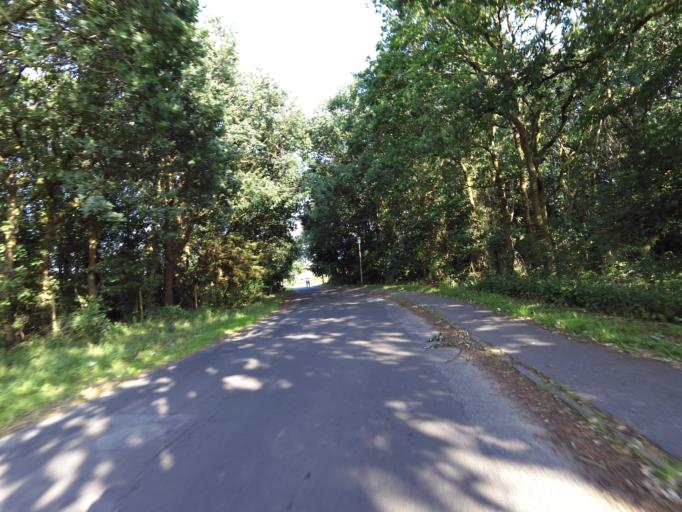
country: DE
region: Lower Saxony
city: Nordholz
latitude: 53.8239
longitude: 8.5874
